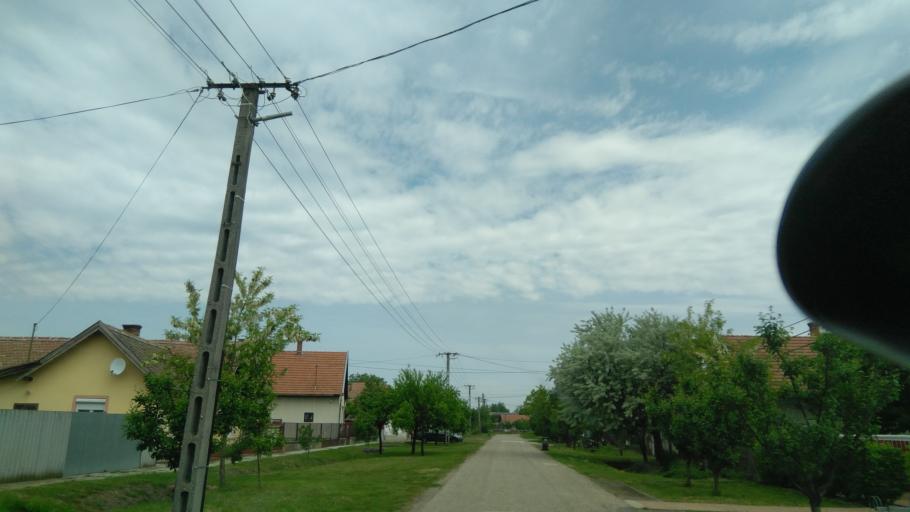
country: HU
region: Bekes
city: Fuzesgyarmat
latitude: 47.1004
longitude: 21.2141
